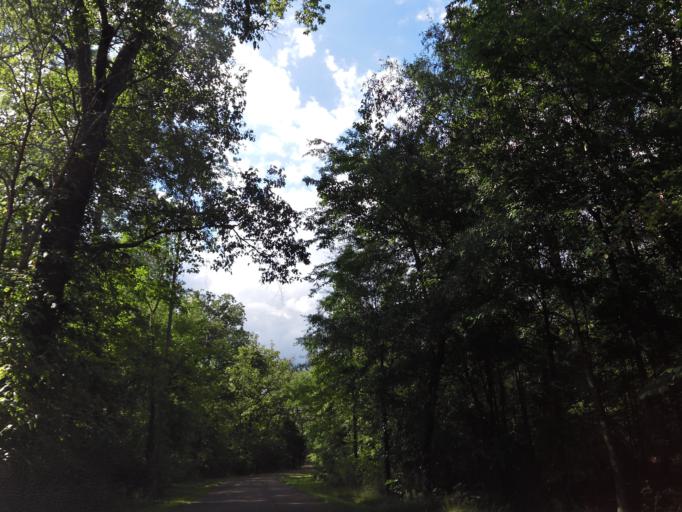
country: US
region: Georgia
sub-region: Walker County
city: Chickamauga
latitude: 34.9027
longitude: -85.2677
